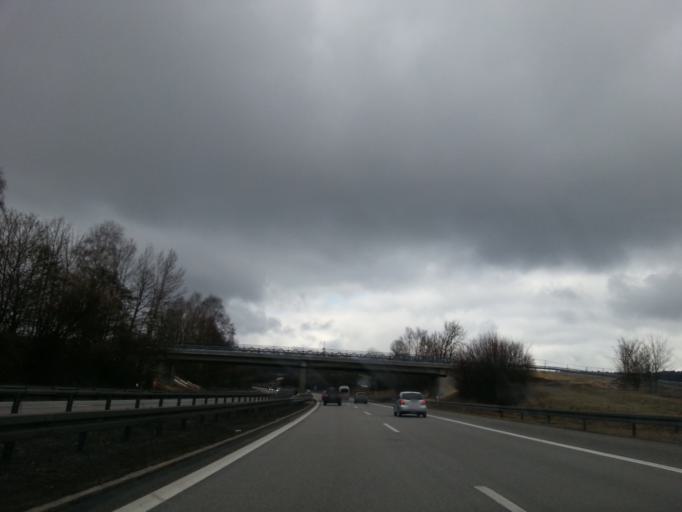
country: DE
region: Bavaria
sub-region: Upper Palatinate
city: Hohenfels
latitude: 49.1608
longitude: 11.8393
